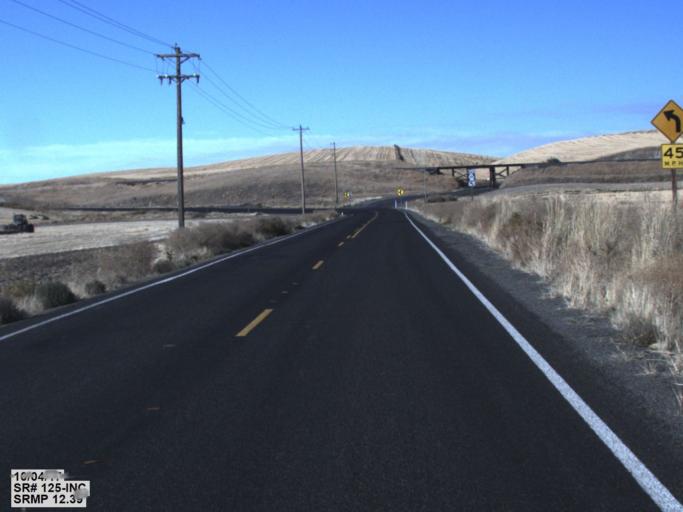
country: US
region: Washington
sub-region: Walla Walla County
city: Walla Walla
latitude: 46.1510
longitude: -118.3726
